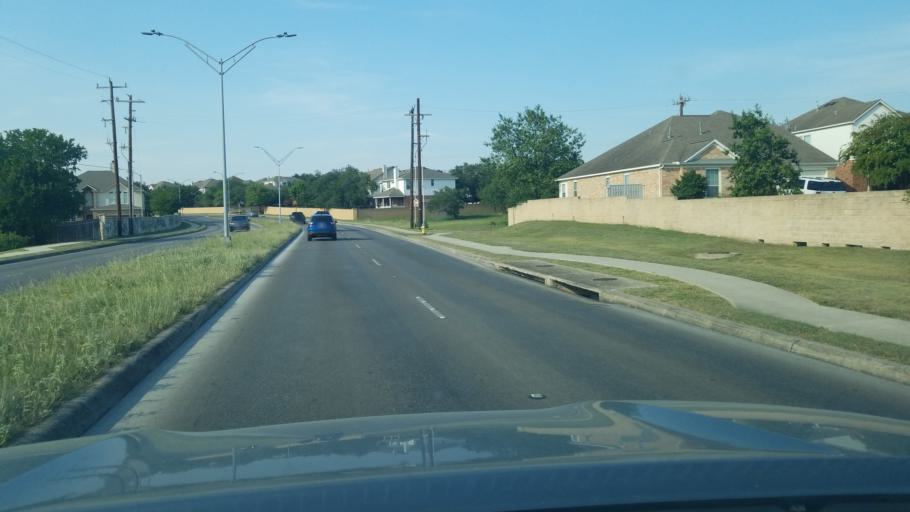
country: US
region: Texas
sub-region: Bexar County
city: Hollywood Park
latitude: 29.6477
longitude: -98.5041
